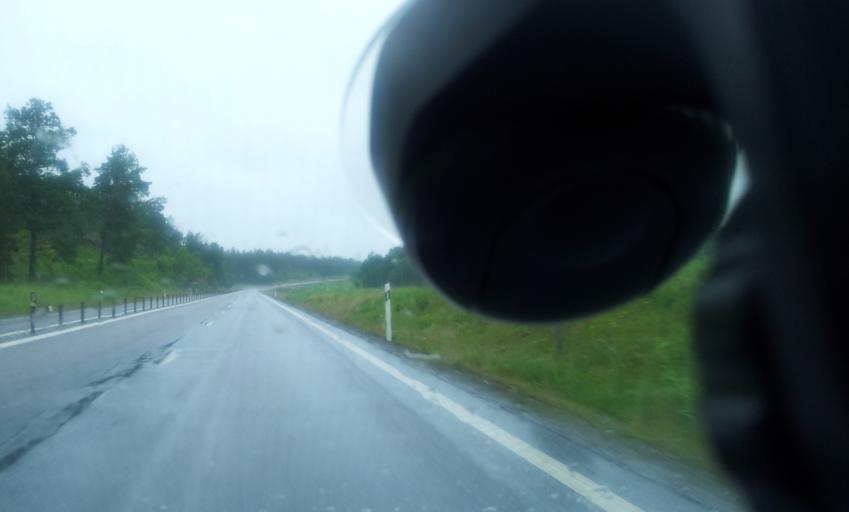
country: SE
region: OEstergoetland
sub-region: Soderkopings Kommun
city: Soederkoeping
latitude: 58.4248
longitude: 16.3893
